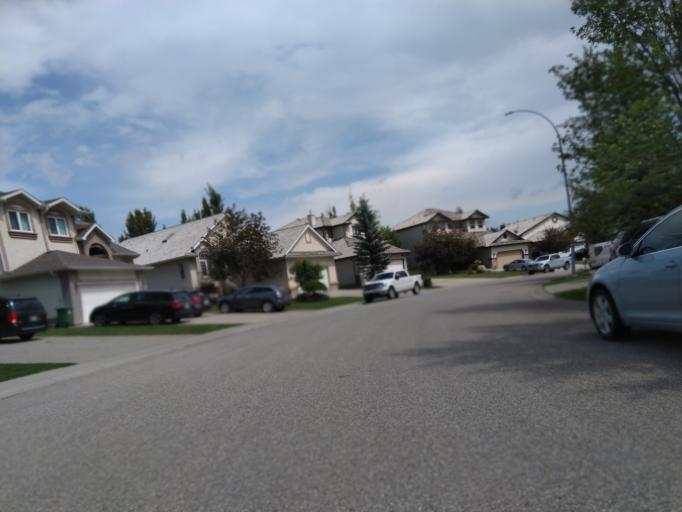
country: CA
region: Alberta
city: Cochrane
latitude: 51.1877
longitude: -114.4991
